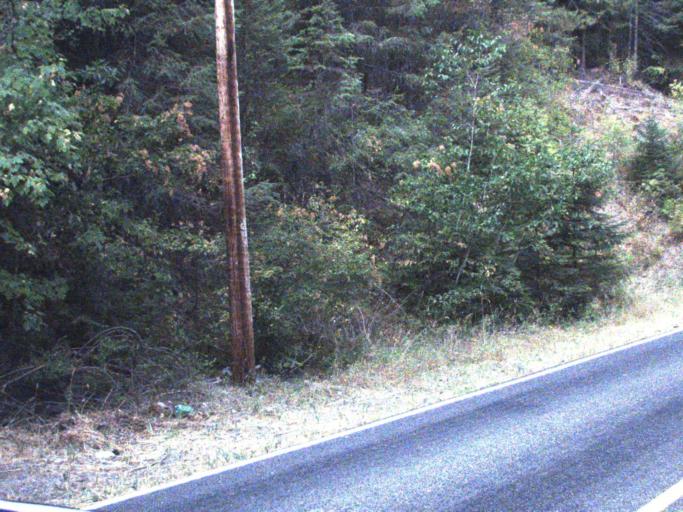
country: US
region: Washington
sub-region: Spokane County
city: Trentwood
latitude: 47.8531
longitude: -117.1646
